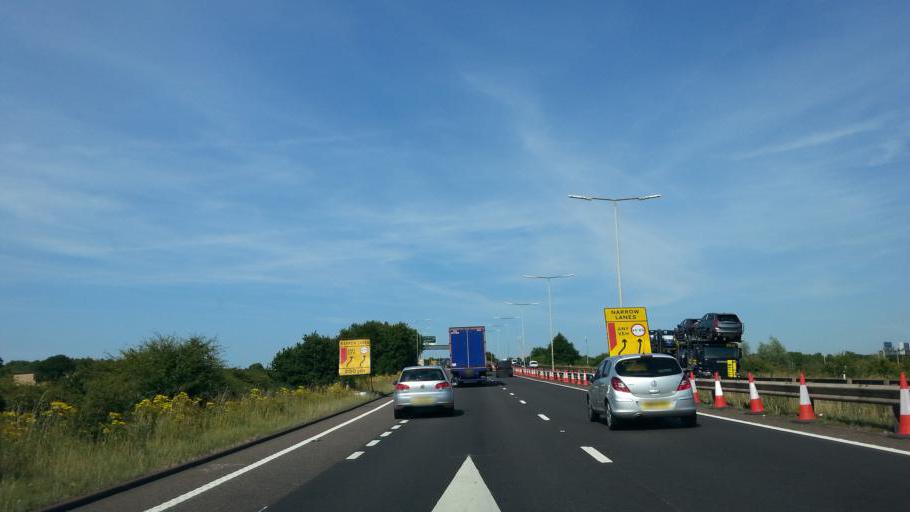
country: GB
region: England
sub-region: Leicestershire
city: Kegworth
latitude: 52.8123
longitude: -1.3110
